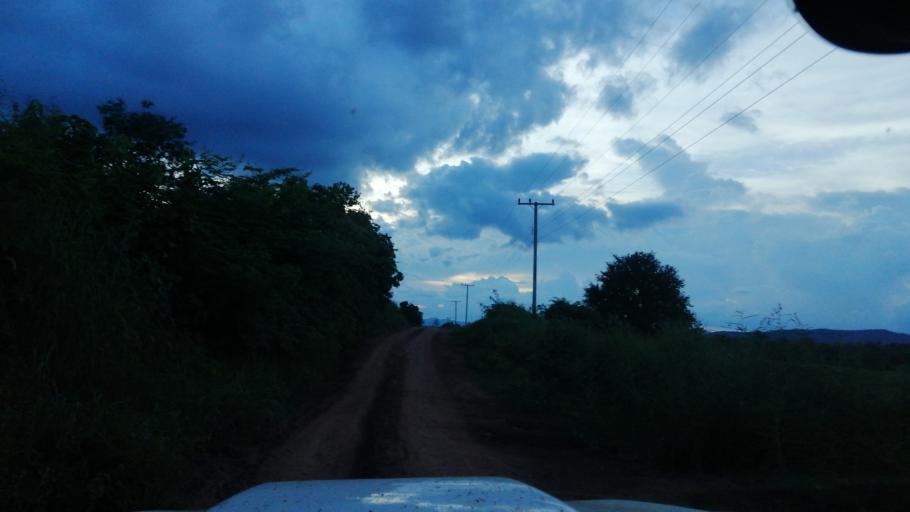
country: TH
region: Uttaradit
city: Ban Khok
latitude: 17.8779
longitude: 101.0669
